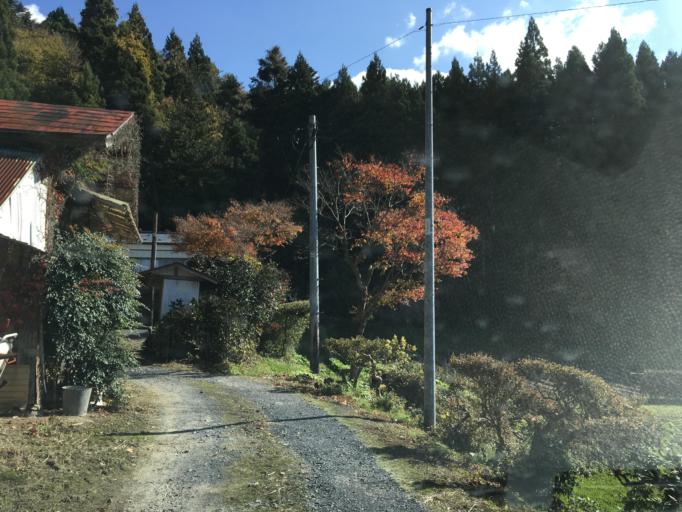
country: JP
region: Iwate
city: Ichinoseki
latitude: 38.9440
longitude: 141.4169
